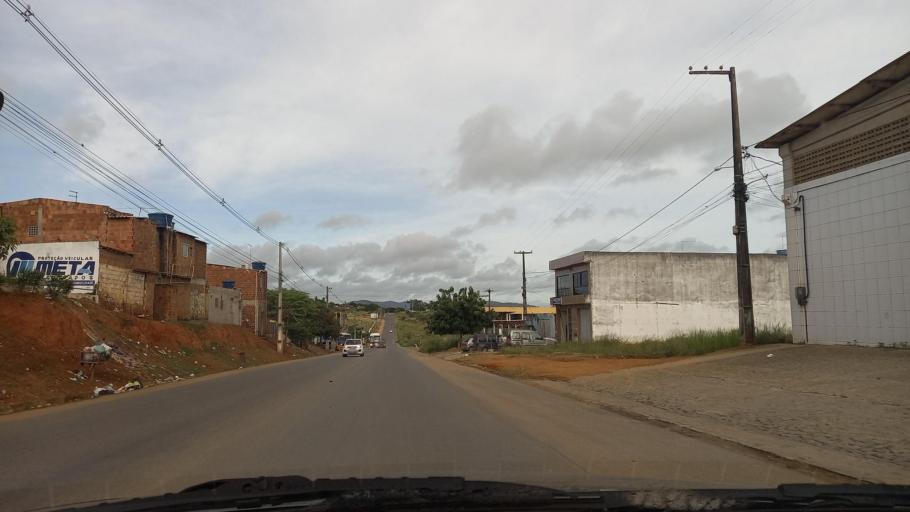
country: BR
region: Pernambuco
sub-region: Vitoria De Santo Antao
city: Vitoria de Santo Antao
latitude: -8.1229
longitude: -35.3349
